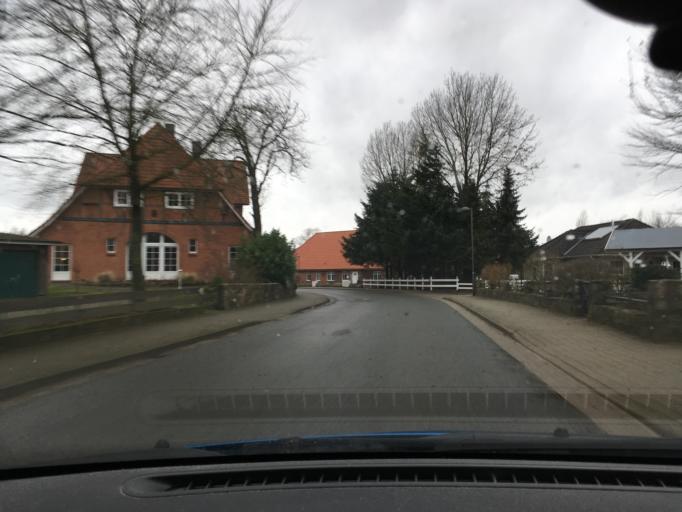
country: DE
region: Mecklenburg-Vorpommern
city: Boizenburg
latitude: 53.3500
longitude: 10.6766
